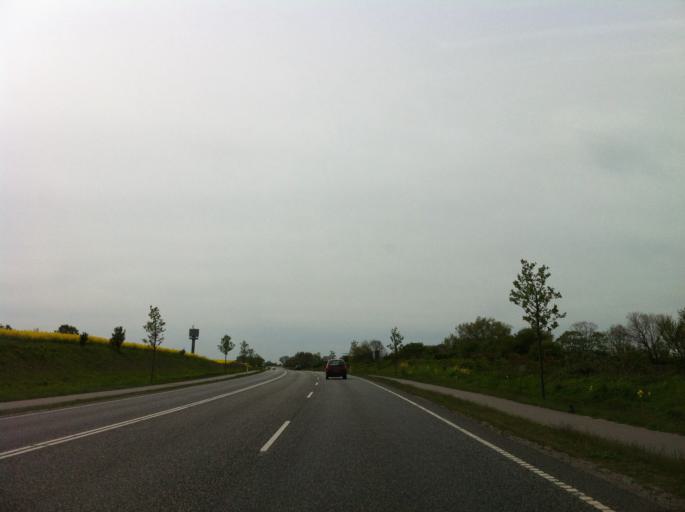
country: DK
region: Zealand
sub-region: Roskilde Kommune
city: Gundsomagle
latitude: 55.6980
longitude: 12.1079
